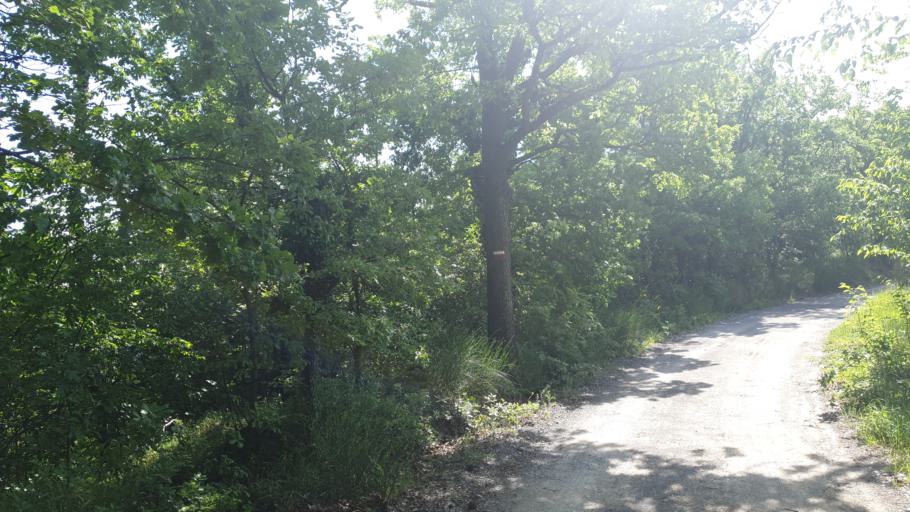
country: IT
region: Emilia-Romagna
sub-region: Provincia di Bologna
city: Sasso Marconi
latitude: 44.3760
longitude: 11.2805
